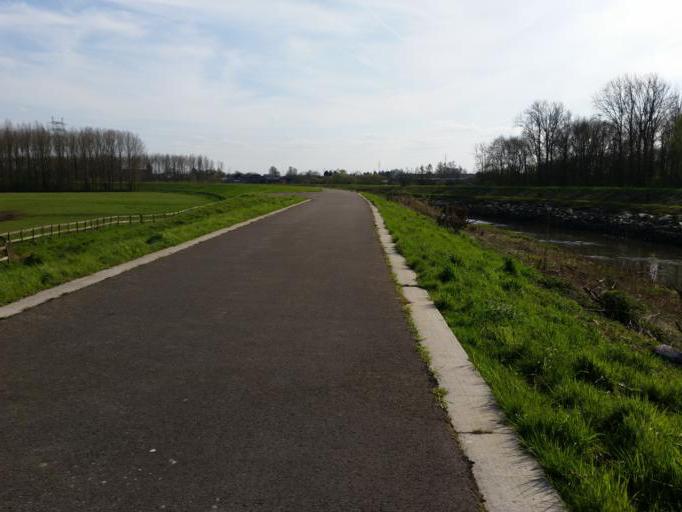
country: BE
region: Flanders
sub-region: Provincie Antwerpen
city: Rumst
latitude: 51.0424
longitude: 4.4199
